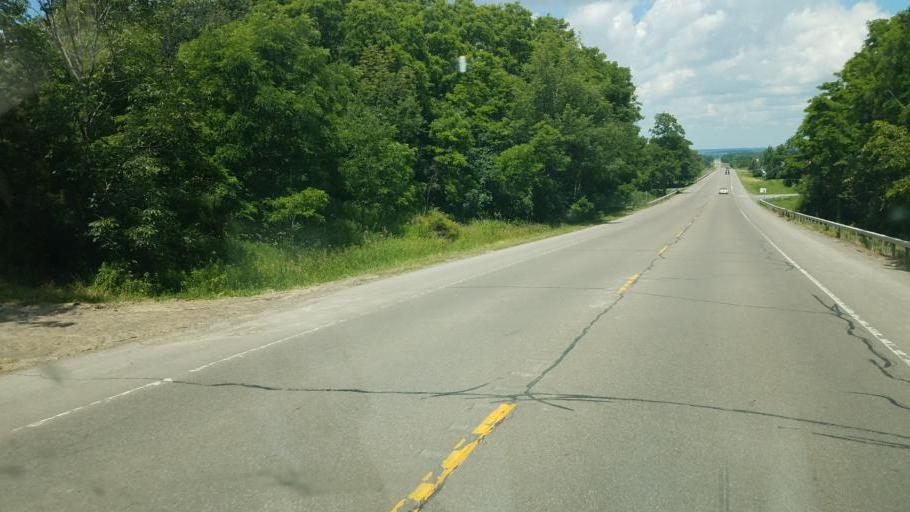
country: US
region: New York
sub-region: Yates County
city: Keuka Park
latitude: 42.5947
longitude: -77.0373
